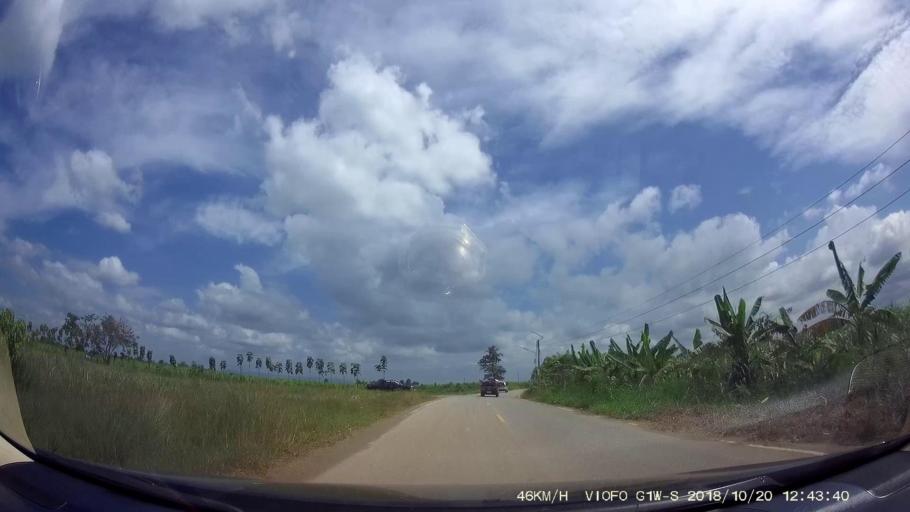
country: TH
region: Chaiyaphum
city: Khon San
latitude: 16.5412
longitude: 101.8628
